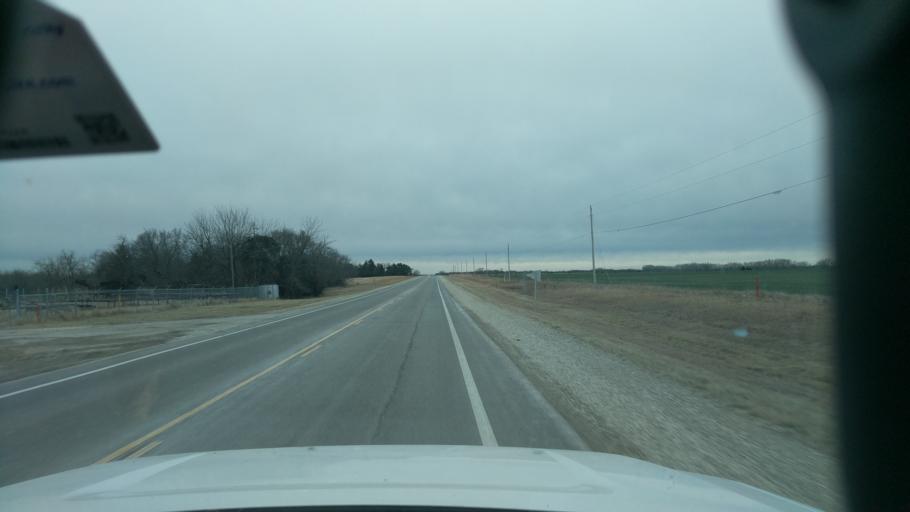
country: US
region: Kansas
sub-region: Marion County
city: Marion
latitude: 38.4846
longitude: -96.9578
